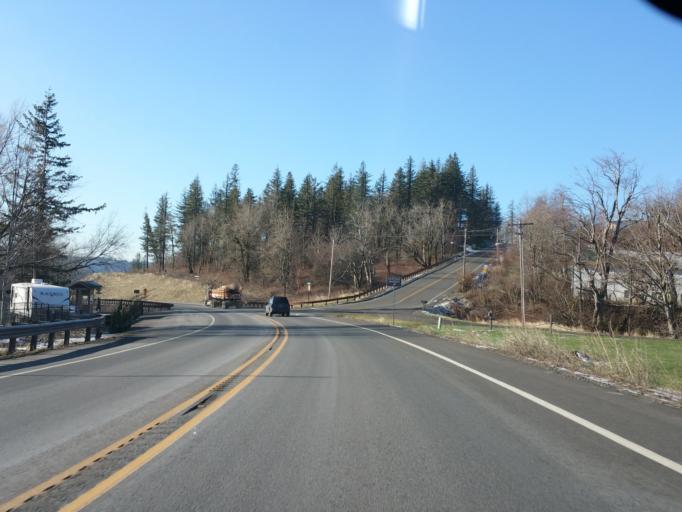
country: US
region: Washington
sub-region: Clark County
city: Washougal
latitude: 45.5635
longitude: -122.2262
